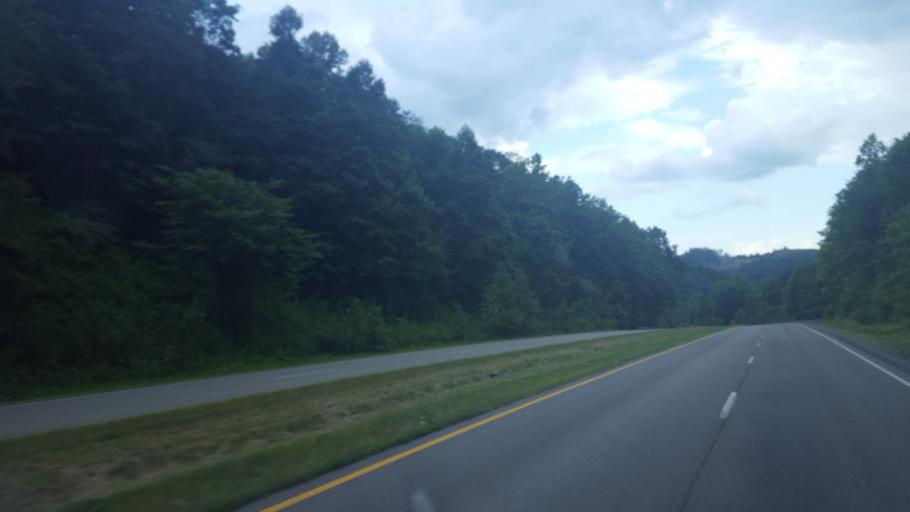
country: US
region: Virginia
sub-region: Wise County
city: Pound
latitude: 37.1215
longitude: -82.6204
